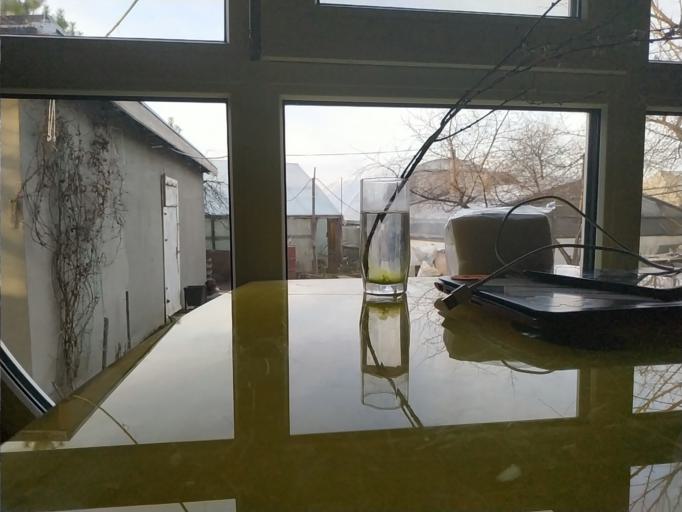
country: RU
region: Republic of Karelia
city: Suoyarvi
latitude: 62.1642
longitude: 32.1347
